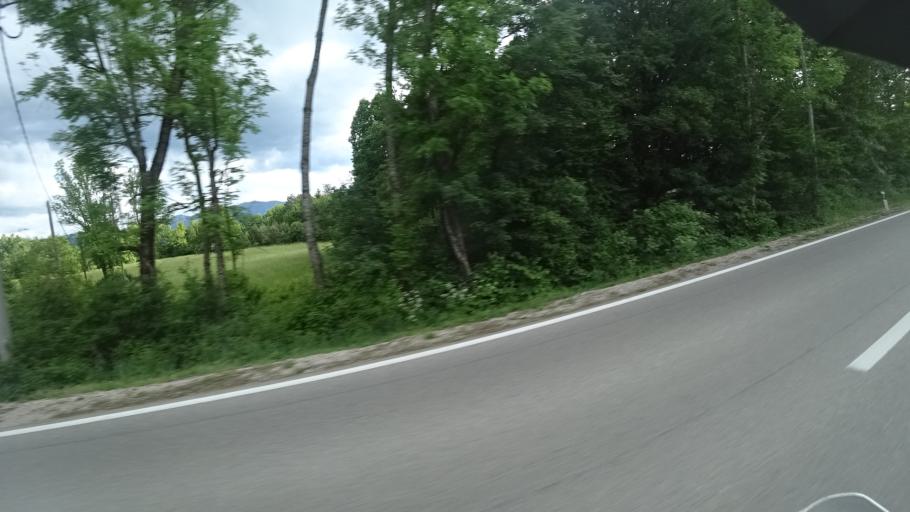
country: HR
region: Licko-Senjska
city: Gospic
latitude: 44.5078
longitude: 15.4402
